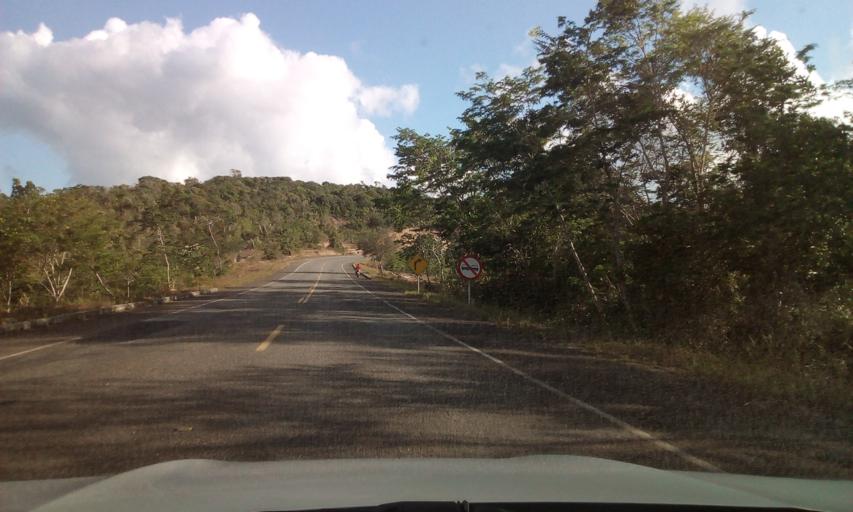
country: BR
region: Bahia
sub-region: Conde
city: Conde
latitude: -12.0870
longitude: -37.7728
